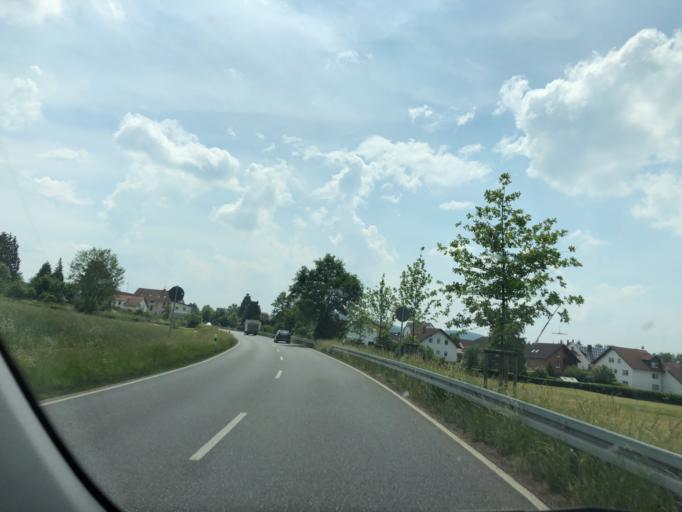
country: DE
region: Hesse
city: Neustadt (Hessen)
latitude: 50.8591
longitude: 9.1225
